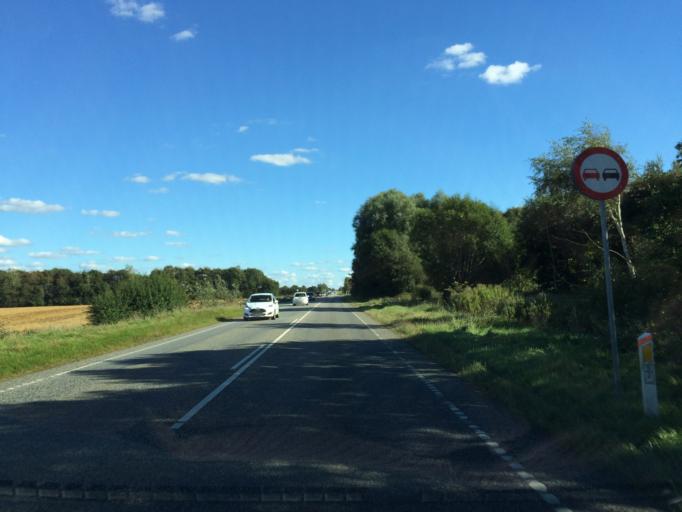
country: DK
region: Central Jutland
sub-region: Holstebro Kommune
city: Holstebro
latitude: 56.3239
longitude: 8.6700
